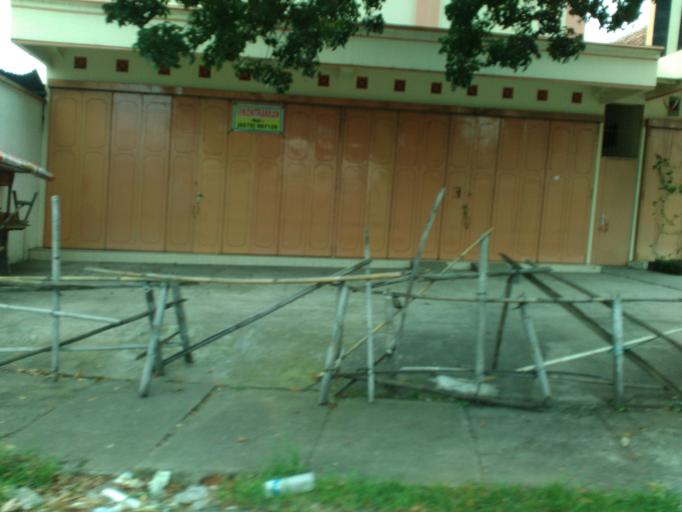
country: ID
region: Central Java
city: Klaten
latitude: -7.6871
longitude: 110.6347
